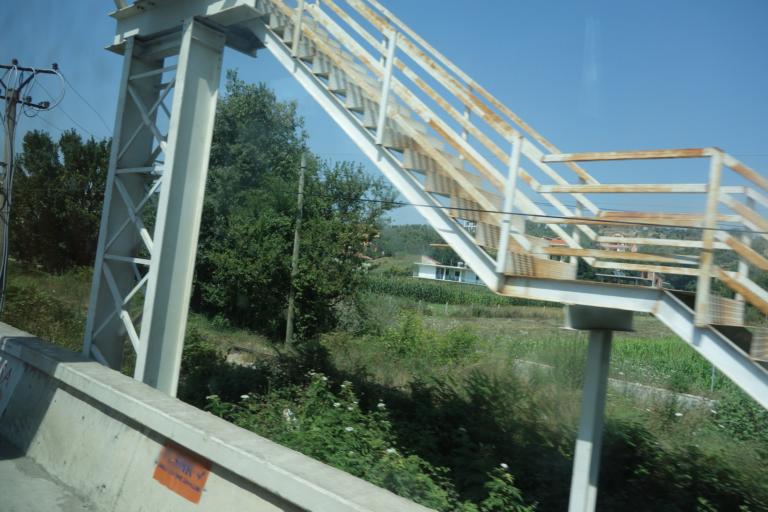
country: AL
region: Tirane
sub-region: Rrethi i Kavajes
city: Golem
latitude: 41.2644
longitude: 19.5241
